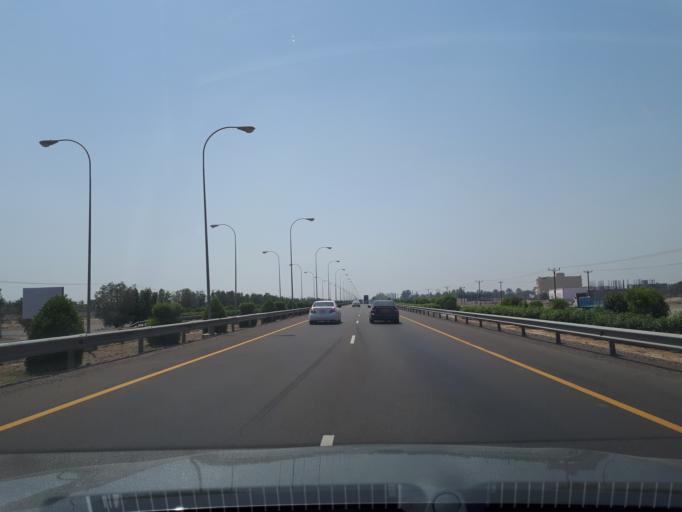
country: OM
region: Al Batinah
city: Al Sohar
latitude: 24.4031
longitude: 56.6591
